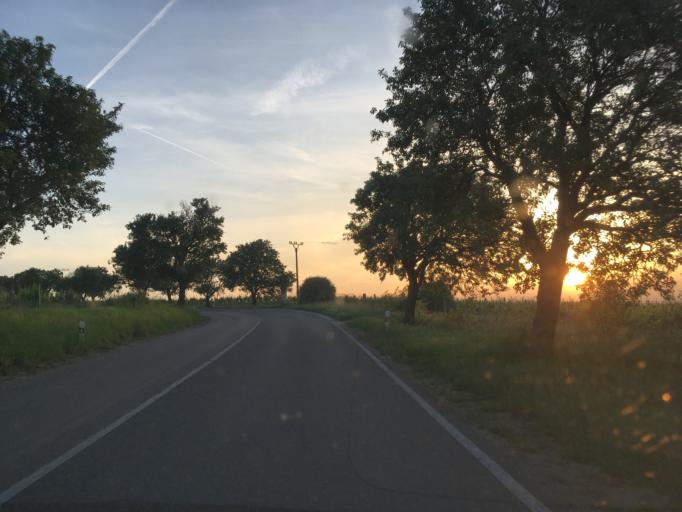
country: CZ
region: South Moravian
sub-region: Okres Breclav
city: Valtice
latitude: 48.7419
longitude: 16.7413
